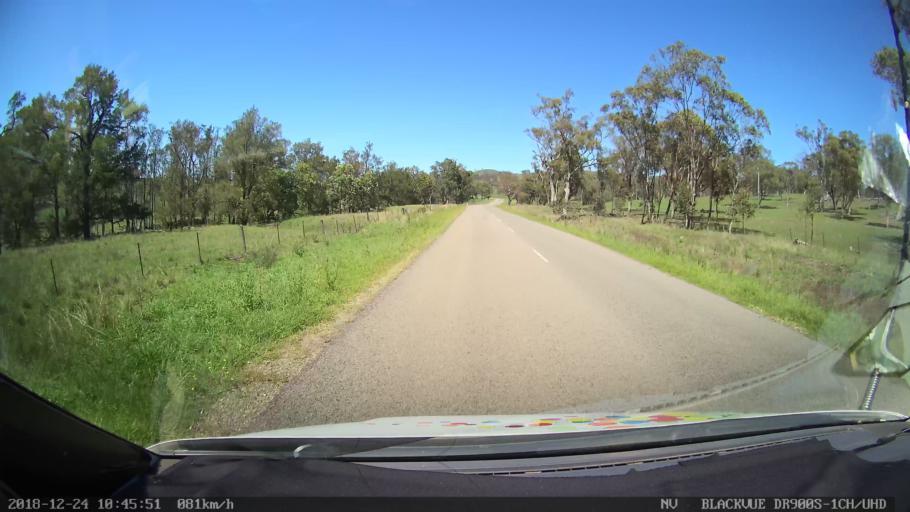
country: AU
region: New South Wales
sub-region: Upper Hunter Shire
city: Merriwa
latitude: -31.9066
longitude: 150.4328
